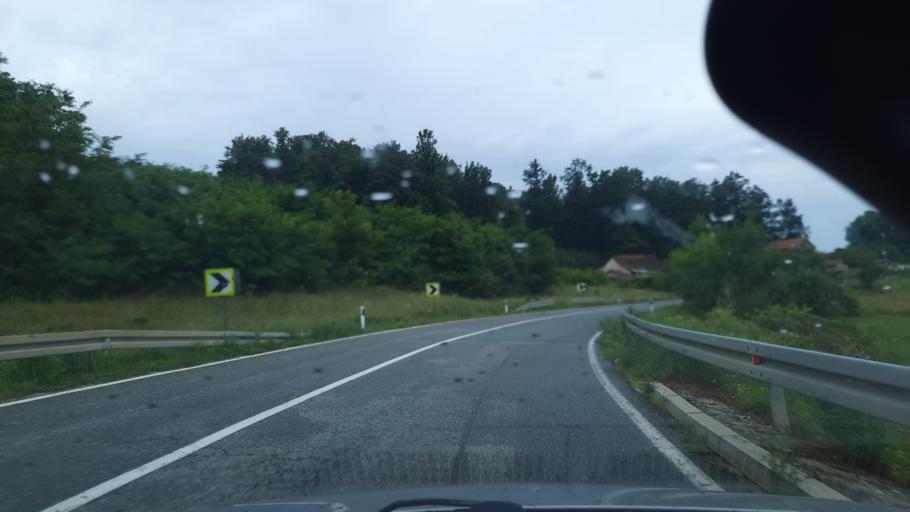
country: RS
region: Central Serbia
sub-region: Sumadijski Okrug
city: Knic
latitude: 43.9086
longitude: 20.7660
